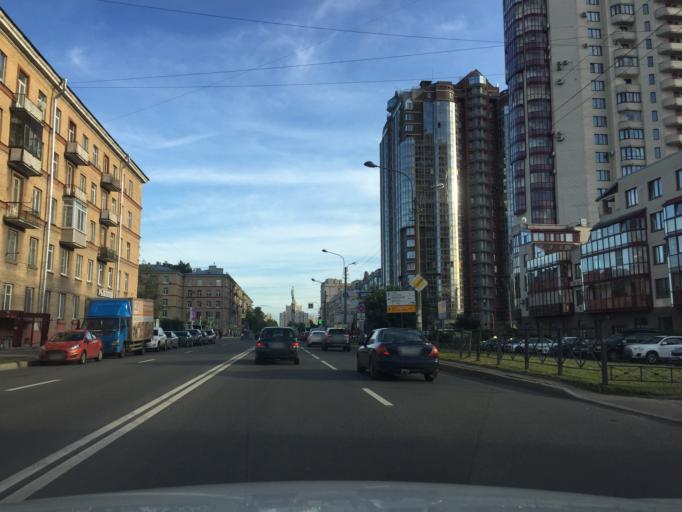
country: RU
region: St.-Petersburg
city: Kupchino
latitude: 59.8532
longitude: 30.3146
